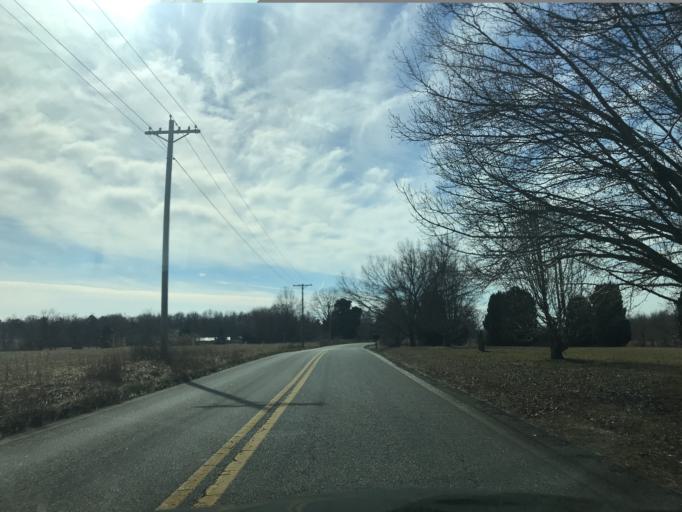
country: US
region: Virginia
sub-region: Prince William County
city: Cherry Hill
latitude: 38.4460
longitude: -77.1929
